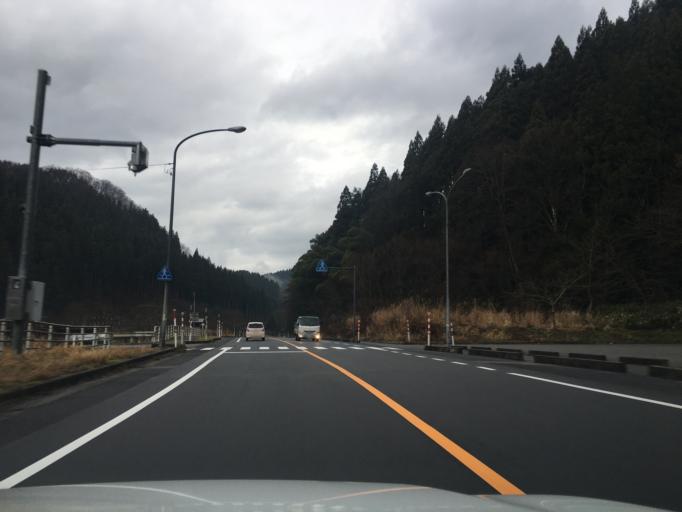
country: JP
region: Niigata
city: Murakami
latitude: 38.4701
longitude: 139.5556
